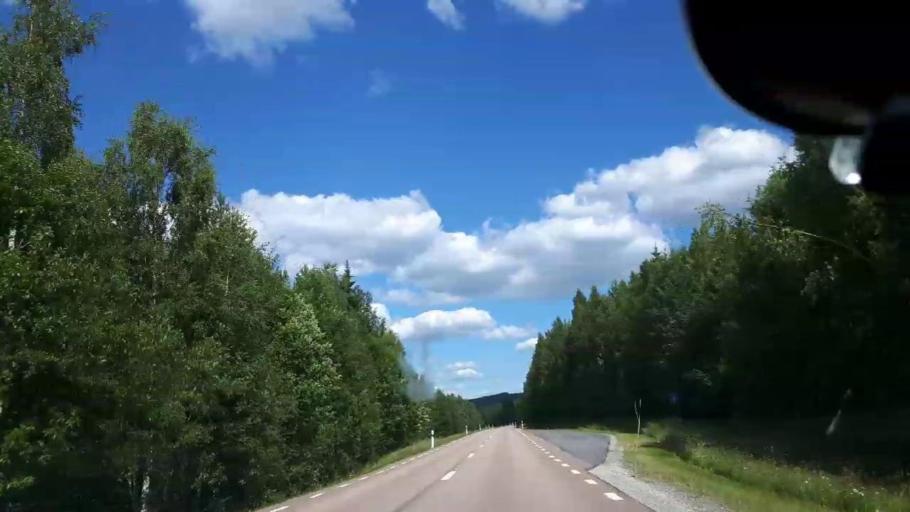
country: SE
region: Jaemtland
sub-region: Ragunda Kommun
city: Hammarstrand
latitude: 62.8945
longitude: 16.6933
